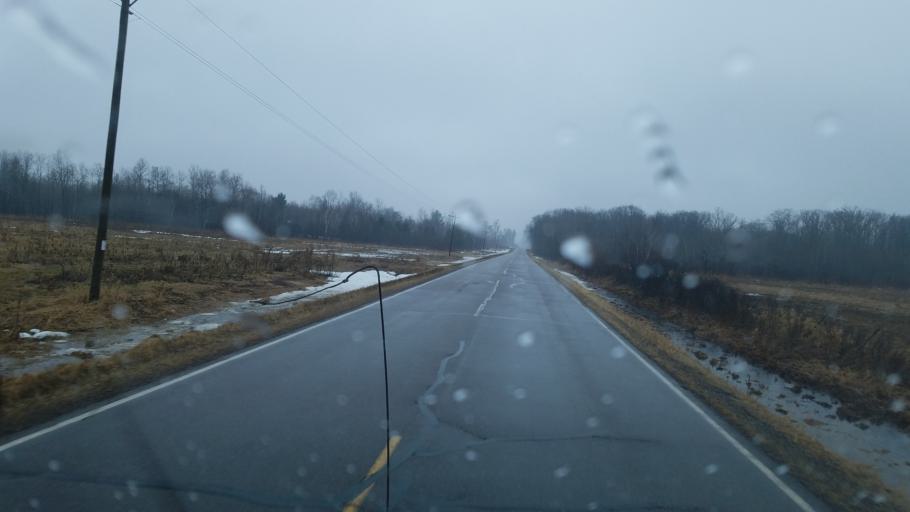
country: US
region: Wisconsin
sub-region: Wood County
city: Marshfield
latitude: 44.4881
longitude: -90.2797
